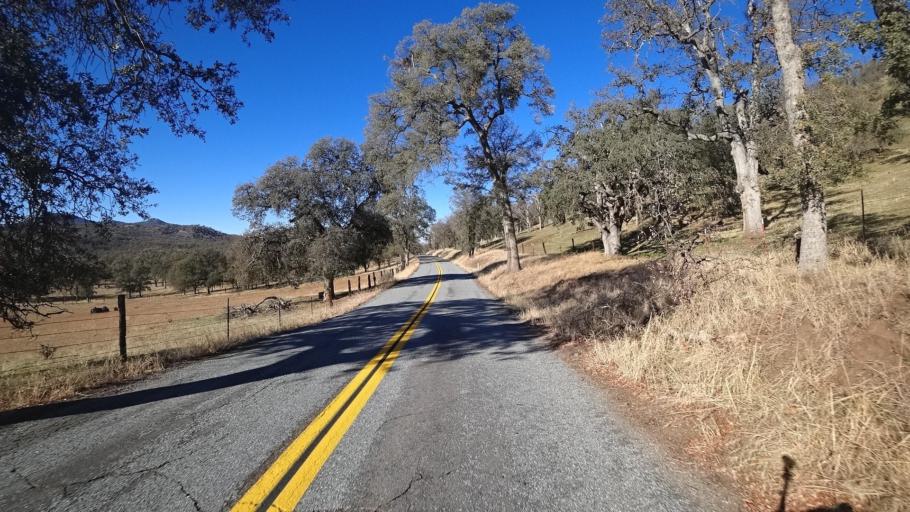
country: US
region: California
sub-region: Kern County
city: Alta Sierra
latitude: 35.7980
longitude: -118.7149
